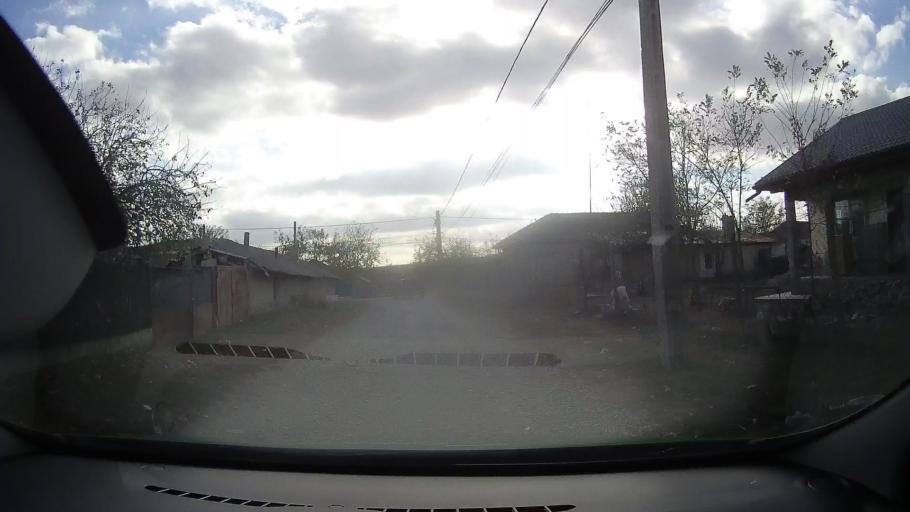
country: RO
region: Constanta
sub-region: Comuna Sacele
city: Sacele
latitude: 44.4891
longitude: 28.6370
